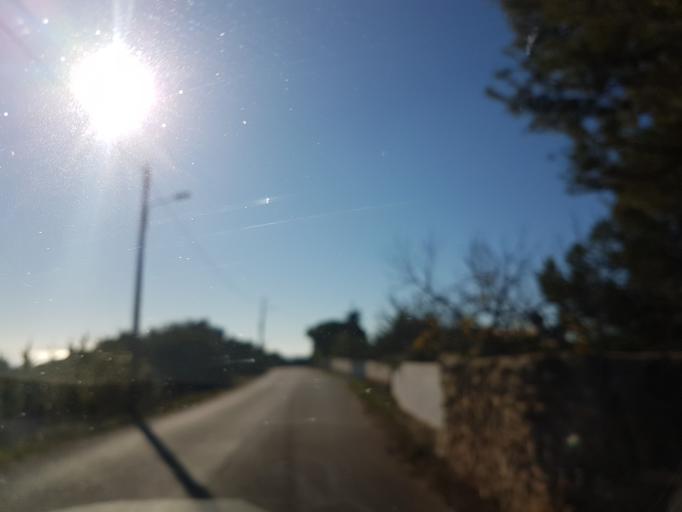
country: PT
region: Faro
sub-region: Lagoa
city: Carvoeiro
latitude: 37.0935
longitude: -8.4193
